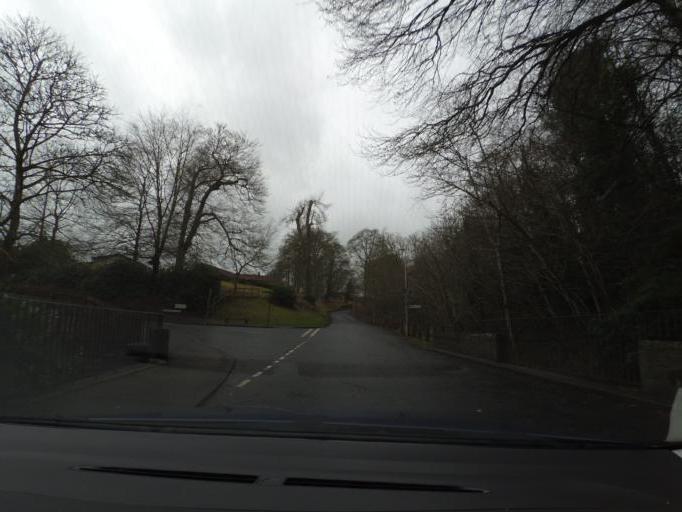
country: GB
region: Scotland
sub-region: The Scottish Borders
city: Hawick
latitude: 55.4231
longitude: -2.8036
